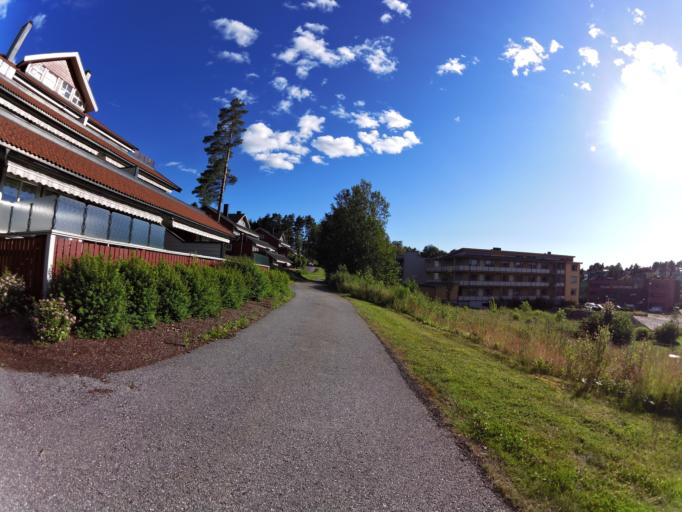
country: NO
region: Ostfold
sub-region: Fredrikstad
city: Fredrikstad
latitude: 59.2229
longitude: 10.9548
